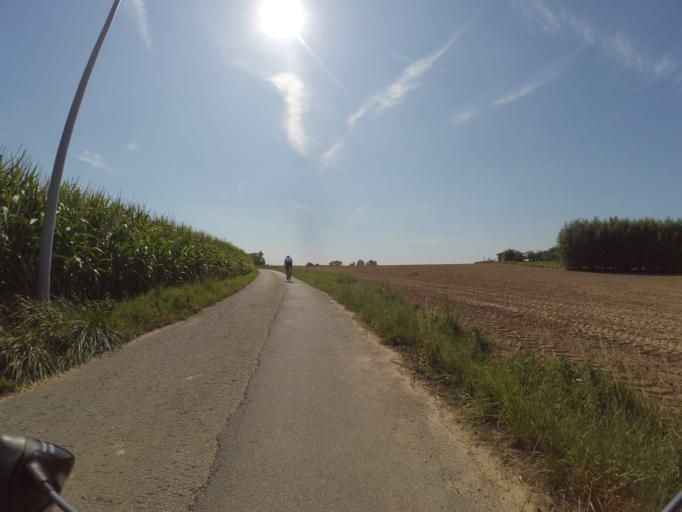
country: BE
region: Flanders
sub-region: Provincie Oost-Vlaanderen
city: Ronse
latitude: 50.7538
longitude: 3.5449
